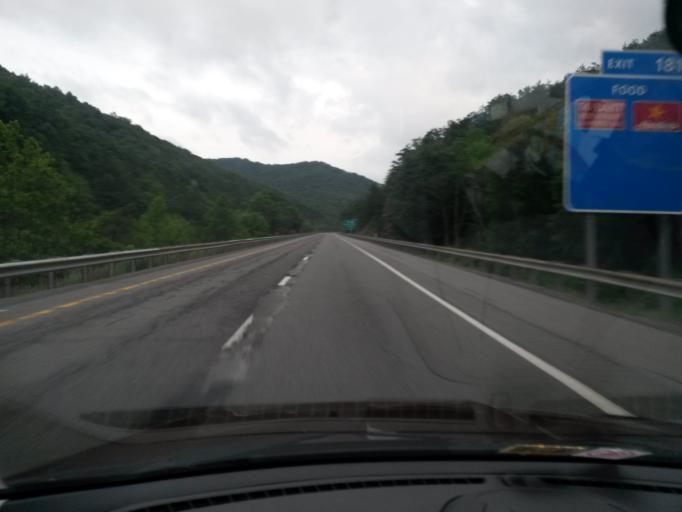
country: US
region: West Virginia
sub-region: Greenbrier County
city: White Sulphur Springs
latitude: 37.7885
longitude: -80.2614
